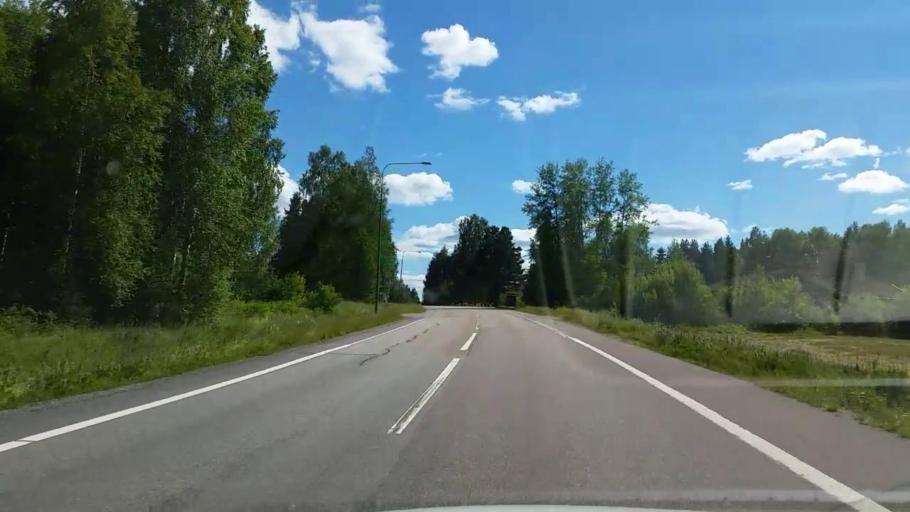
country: SE
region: Dalarna
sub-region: Faluns Kommun
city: Svardsjo
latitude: 60.8292
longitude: 15.7602
